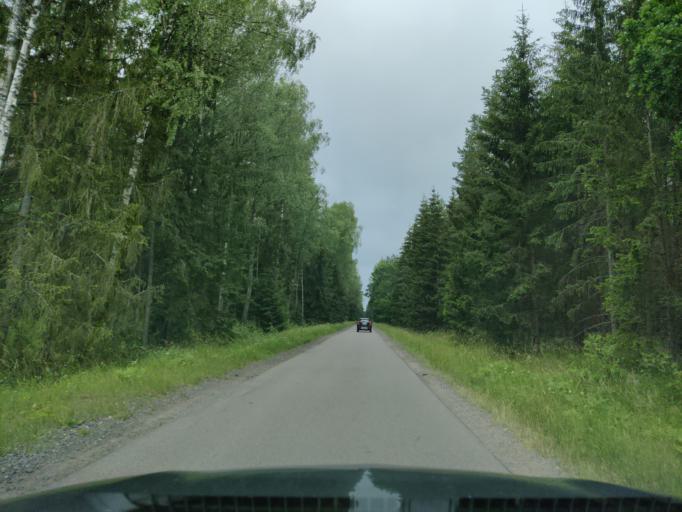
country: PL
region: Warmian-Masurian Voivodeship
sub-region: Powiat piski
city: Ruciane-Nida
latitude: 53.5498
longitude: 21.4647
